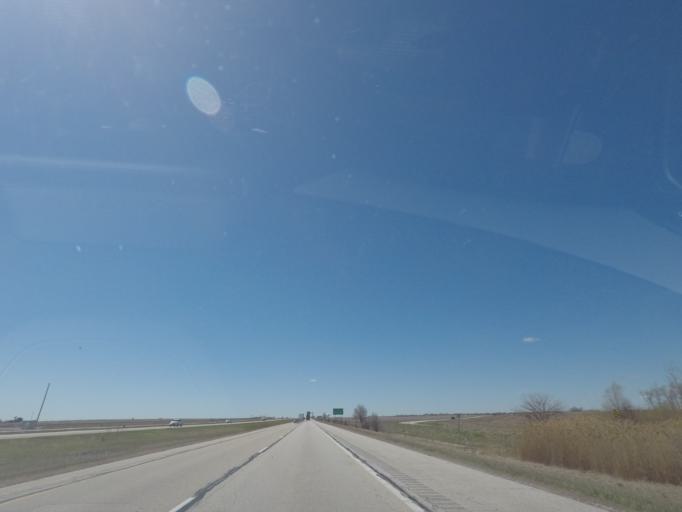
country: US
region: Illinois
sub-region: McLean County
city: Normal
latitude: 40.5479
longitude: -88.9249
